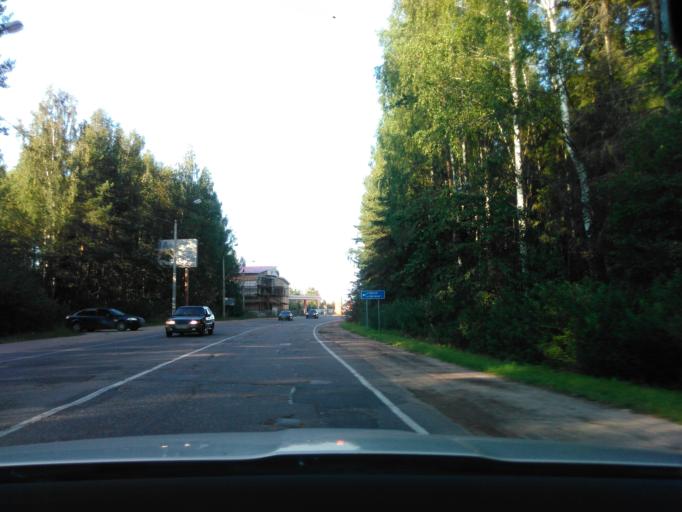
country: RU
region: Tverskaya
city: Konakovo
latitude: 56.6768
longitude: 36.7455
